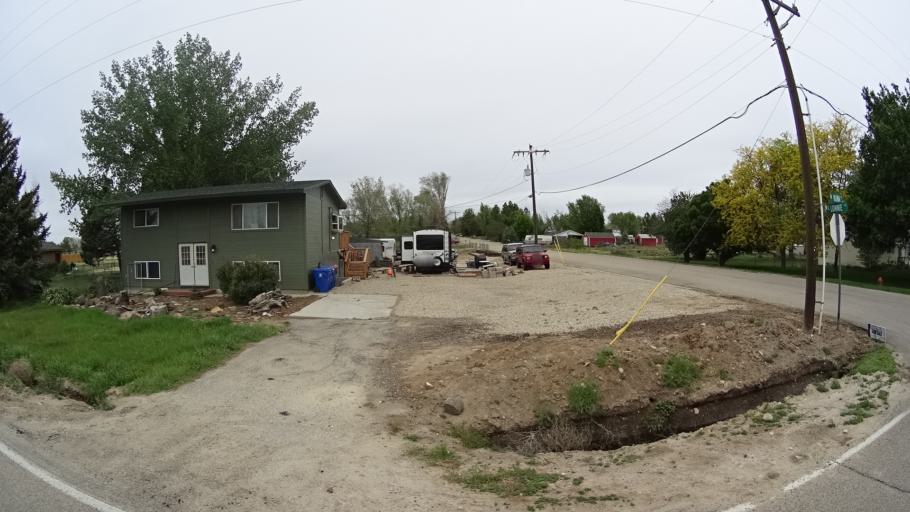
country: US
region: Idaho
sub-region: Ada County
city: Kuna
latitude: 43.4883
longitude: -116.3020
